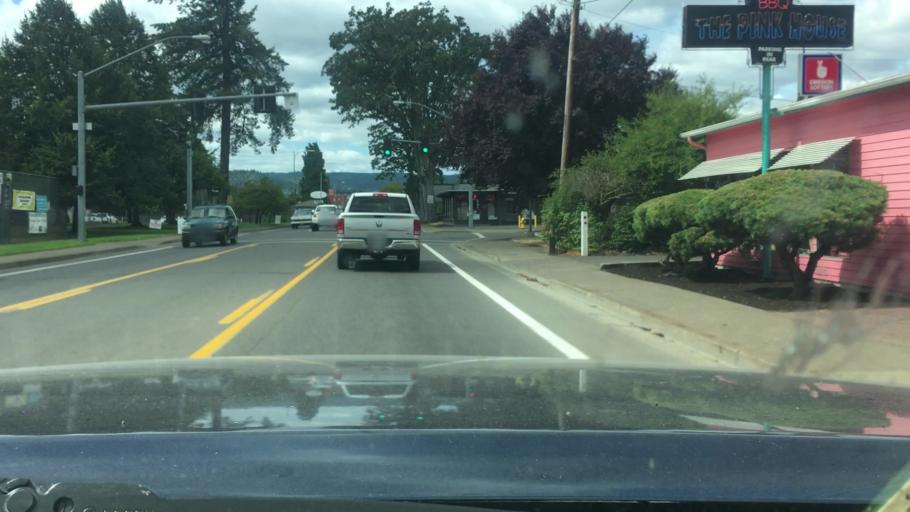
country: US
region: Oregon
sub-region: Lane County
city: Cottage Grove
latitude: 43.7973
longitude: -123.0530
